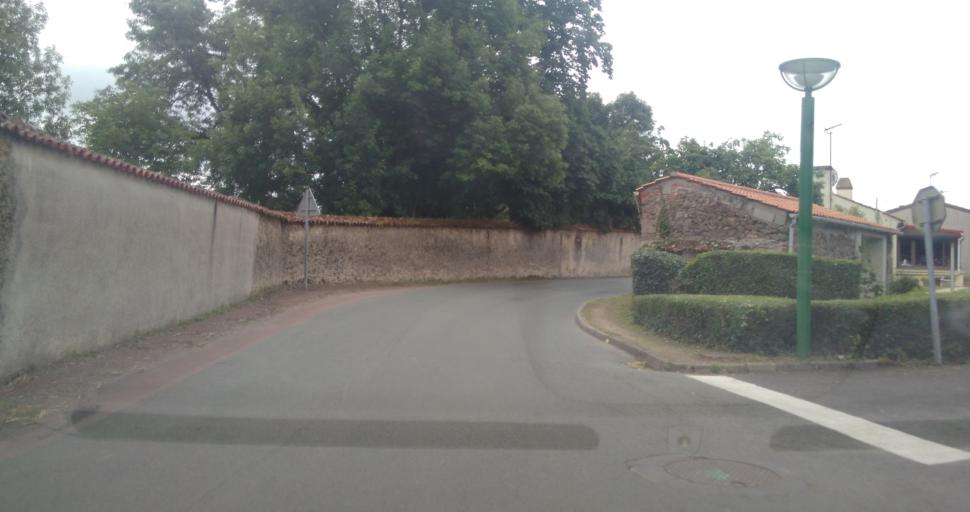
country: FR
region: Pays de la Loire
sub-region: Departement de la Vendee
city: La Chaize-le-Vicomte
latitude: 46.6748
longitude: -1.2948
